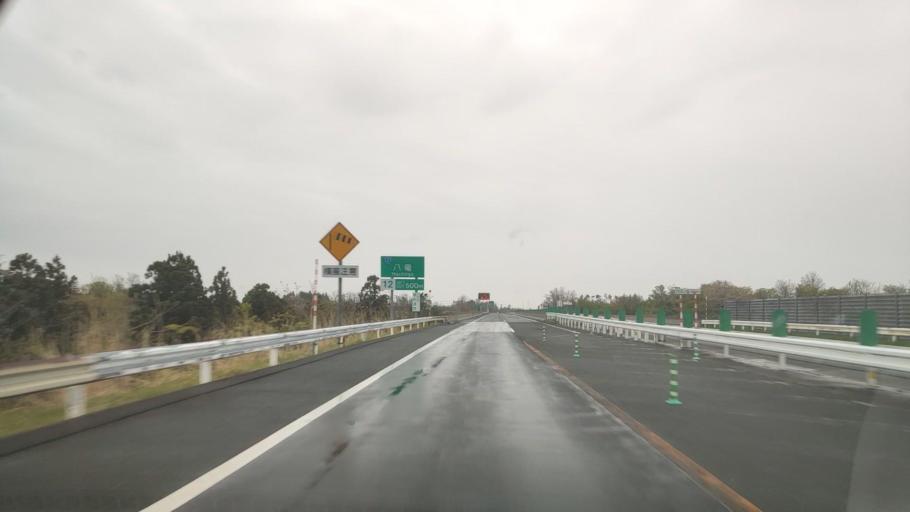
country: JP
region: Akita
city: Noshiromachi
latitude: 40.1264
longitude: 140.0124
